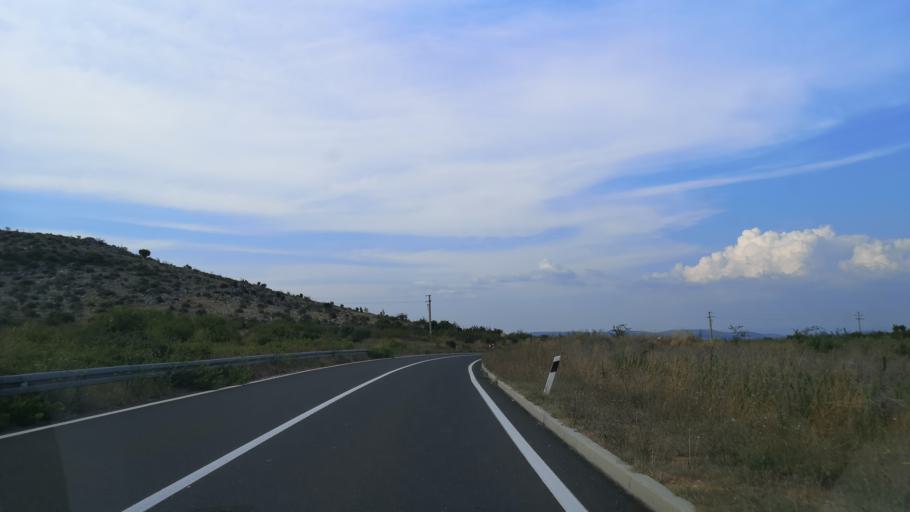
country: HR
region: Sibensko-Kniniska
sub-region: Grad Sibenik
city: Pirovac
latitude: 43.8756
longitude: 15.7409
